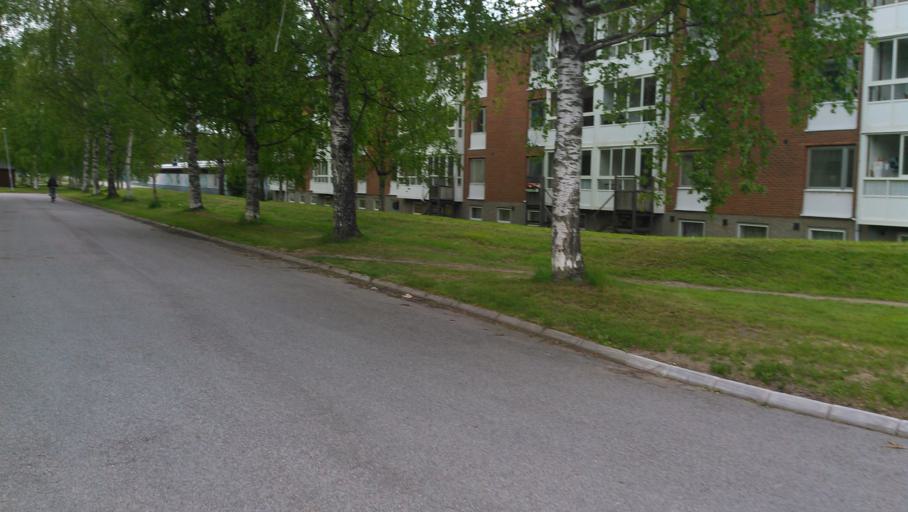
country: SE
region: Vaesterbotten
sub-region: Umea Kommun
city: Umea
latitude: 63.8080
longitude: 20.3149
